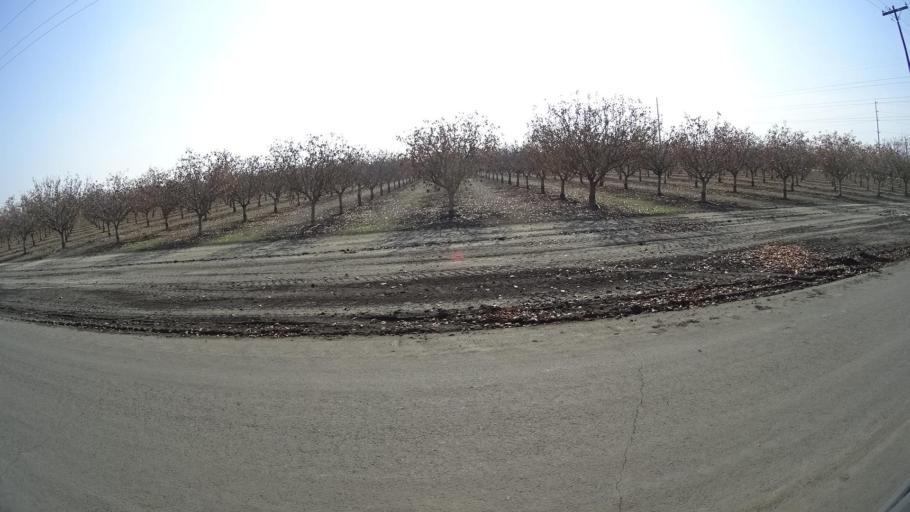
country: US
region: California
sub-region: Kern County
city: Buttonwillow
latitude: 35.3690
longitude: -119.4473
